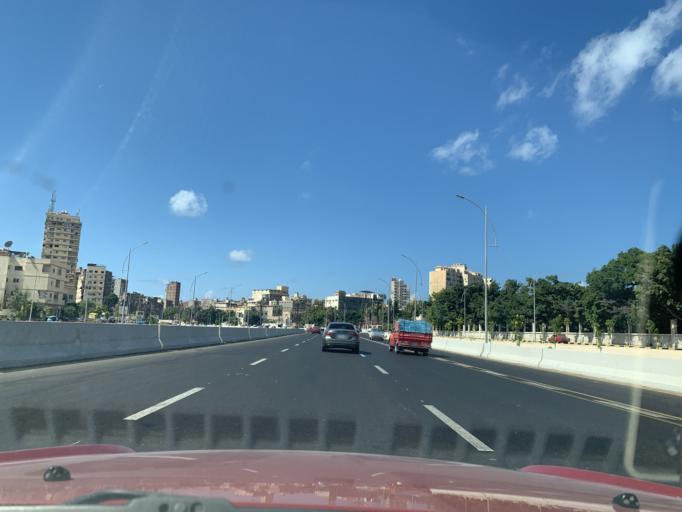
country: EG
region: Alexandria
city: Alexandria
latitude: 31.2016
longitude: 29.9448
